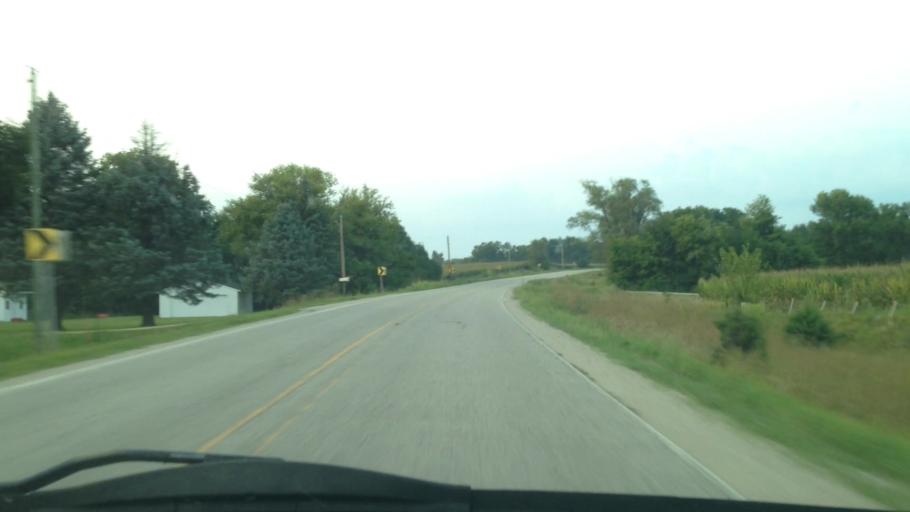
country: US
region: Iowa
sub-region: Benton County
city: Urbana
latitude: 42.1555
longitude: -91.8776
